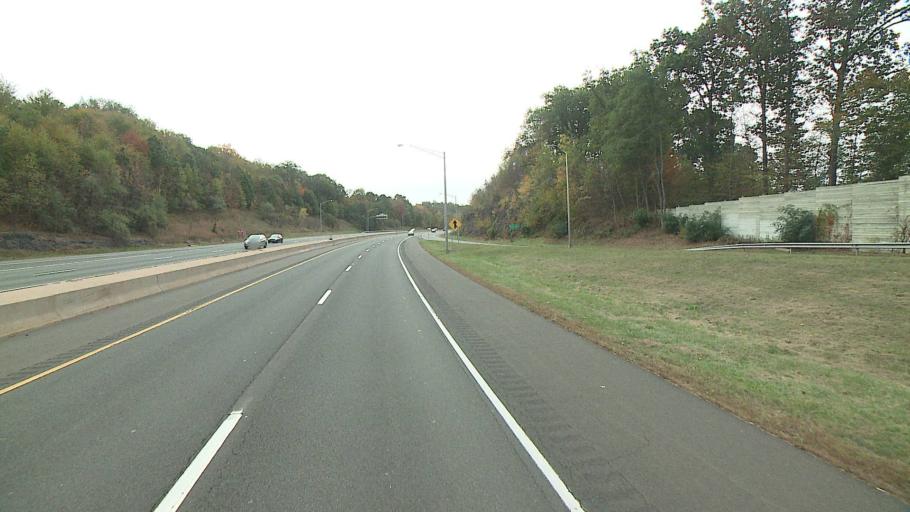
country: US
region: Connecticut
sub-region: Hartford County
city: Newington
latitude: 41.7118
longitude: -72.7621
